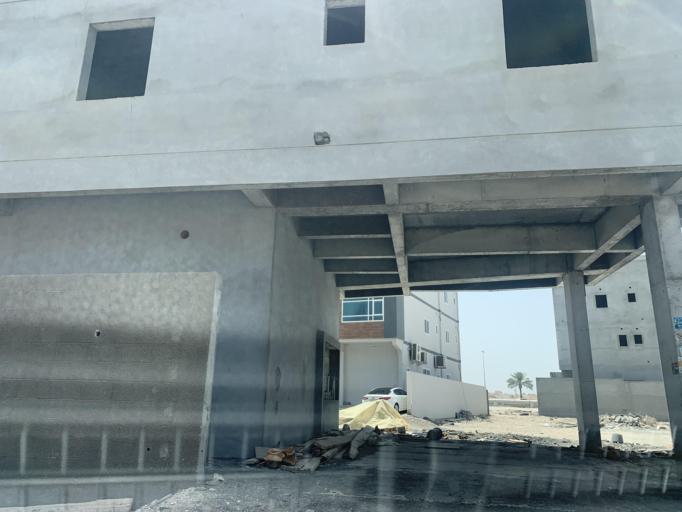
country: BH
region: Central Governorate
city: Madinat Hamad
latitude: 26.1434
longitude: 50.5025
